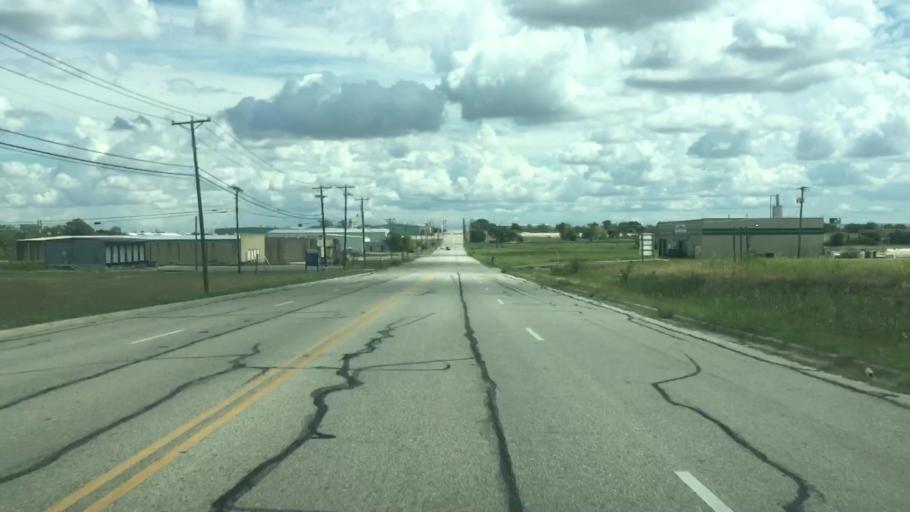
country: US
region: Texas
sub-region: Bell County
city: Temple
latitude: 31.1301
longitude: -97.3545
